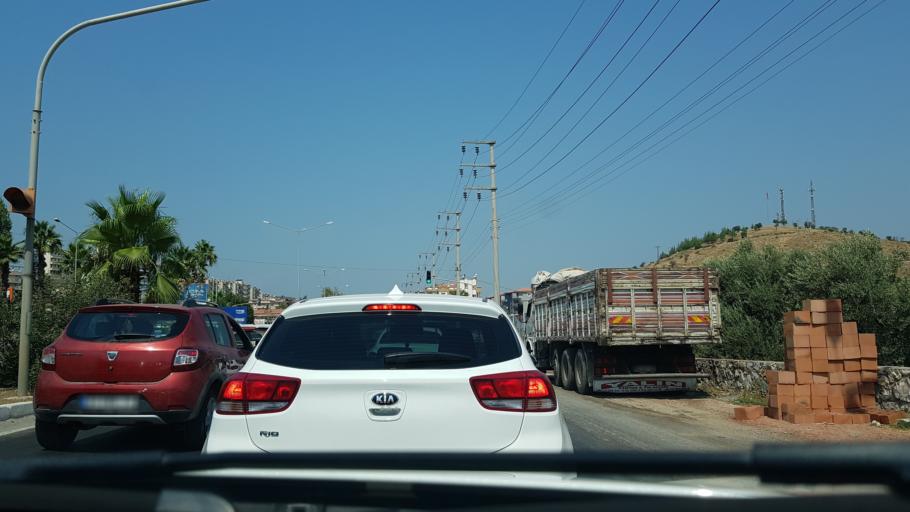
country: TR
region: Mugla
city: Milas
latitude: 37.3262
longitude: 27.7777
